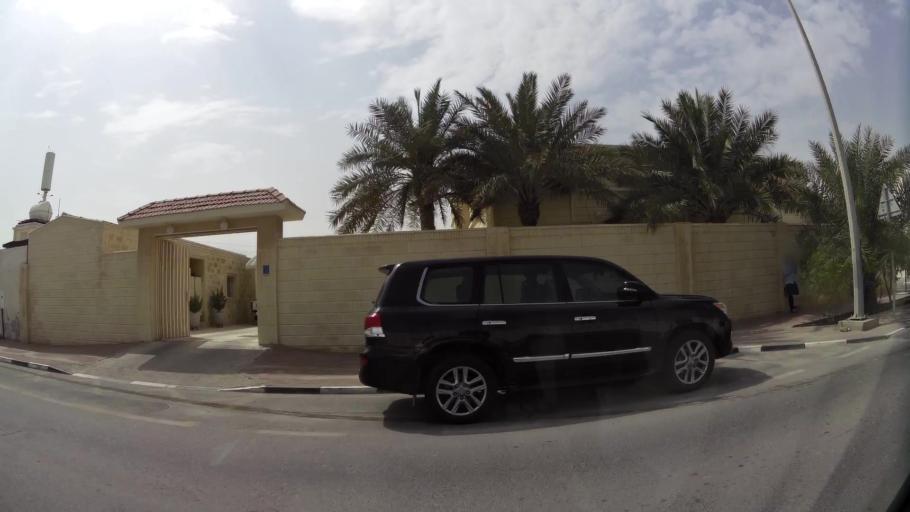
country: QA
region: Baladiyat ad Dawhah
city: Doha
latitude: 25.3022
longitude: 51.4910
